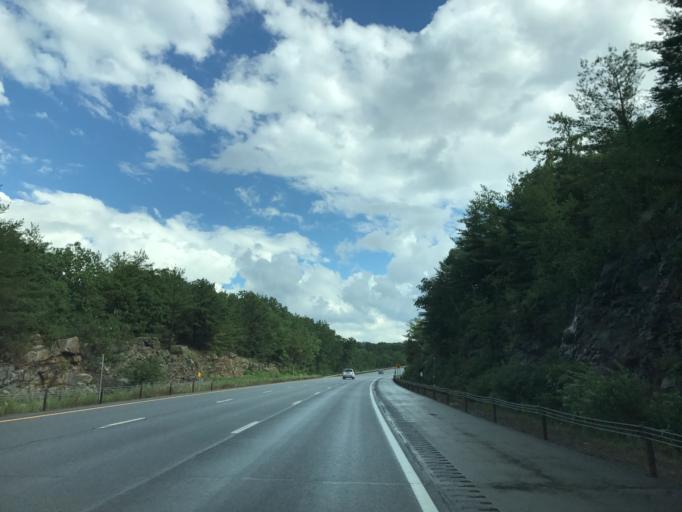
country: US
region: New York
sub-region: Warren County
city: Glens Falls North
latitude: 43.4052
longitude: -73.7155
